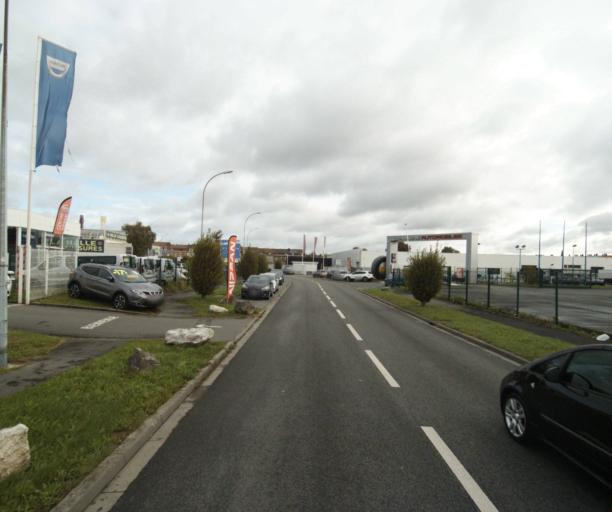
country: FR
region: Nord-Pas-de-Calais
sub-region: Departement du Nord
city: Lomme
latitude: 50.6444
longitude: 3.0090
